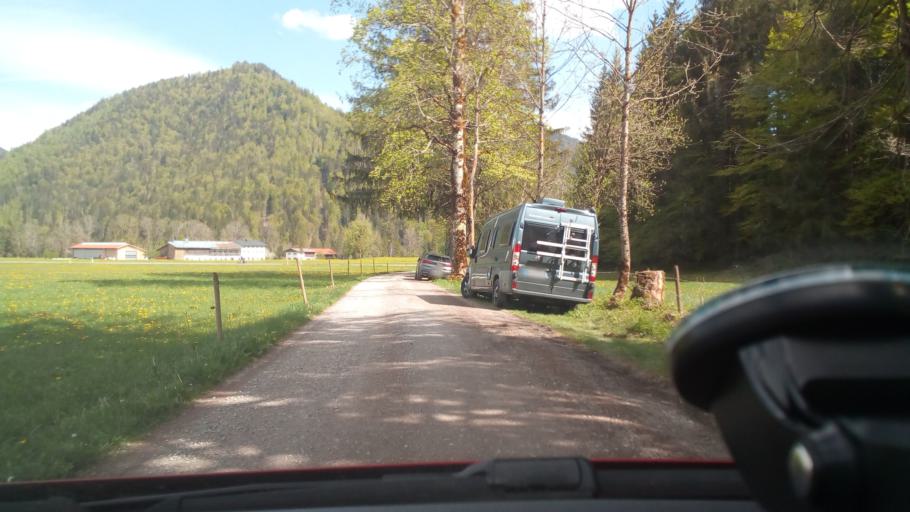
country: DE
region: Bavaria
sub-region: Upper Bavaria
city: Jachenau
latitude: 47.6173
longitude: 11.4997
